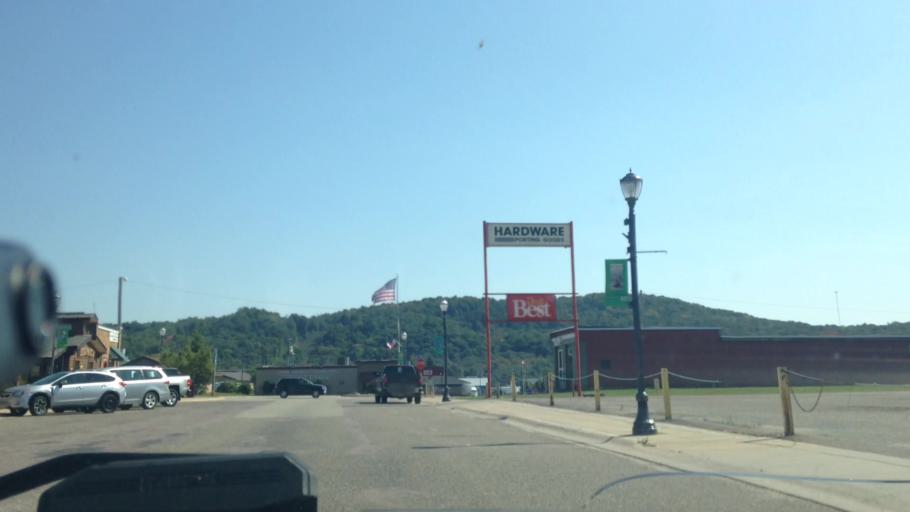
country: US
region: Michigan
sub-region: Alger County
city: Munising
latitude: 46.4093
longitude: -86.6515
